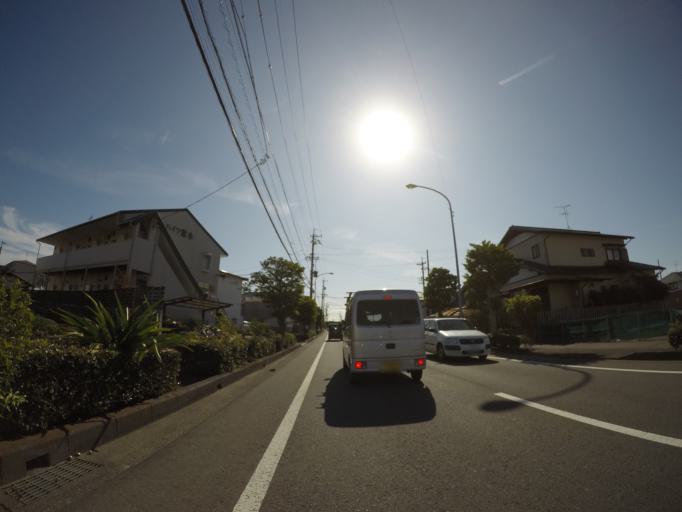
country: JP
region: Shizuoka
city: Shizuoka-shi
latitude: 34.9672
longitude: 138.4226
